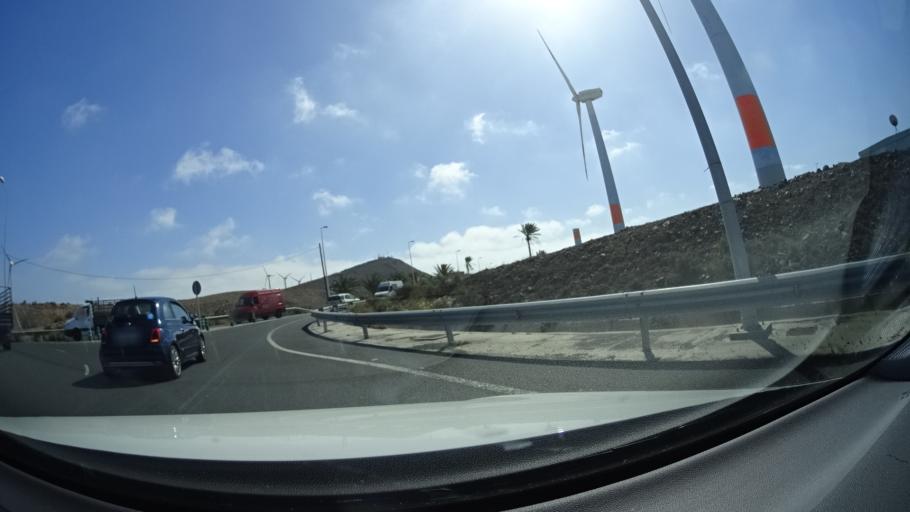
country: ES
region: Canary Islands
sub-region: Provincia de Las Palmas
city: Cruce de Arinaga
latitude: 27.8704
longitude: -15.4179
